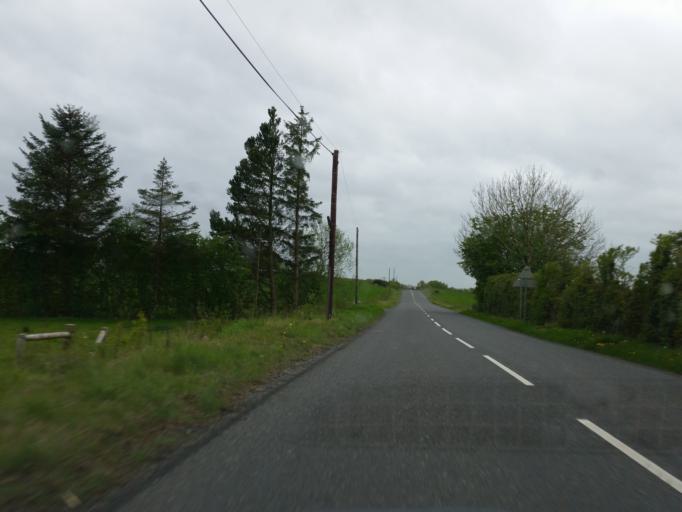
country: GB
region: Northern Ireland
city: Lisnaskea
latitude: 54.2305
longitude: -7.4565
